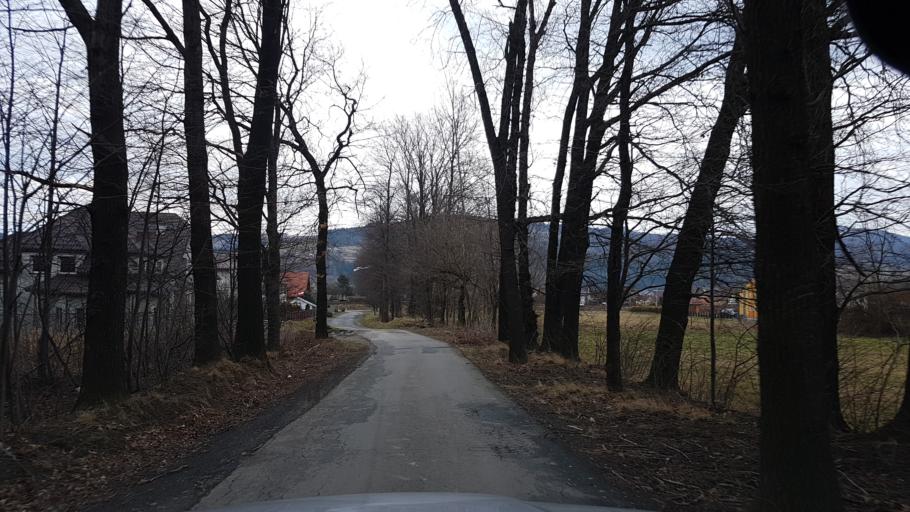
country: PL
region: Lesser Poland Voivodeship
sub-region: Powiat nowosadecki
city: Stary Sacz
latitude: 49.5384
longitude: 20.6429
